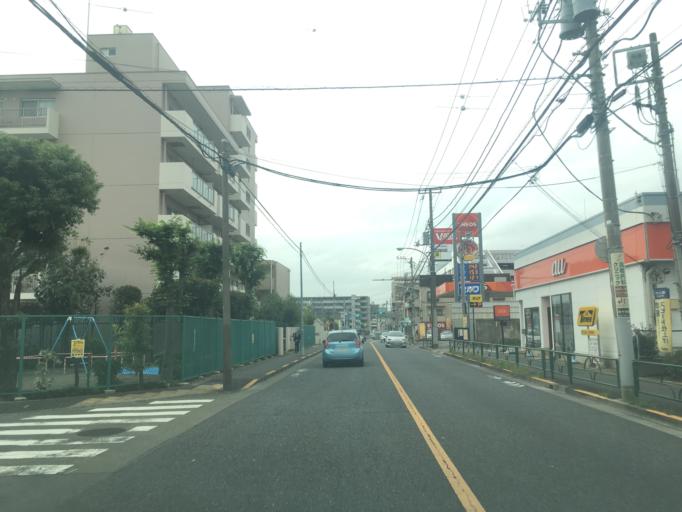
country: JP
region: Tokyo
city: Kokubunji
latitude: 35.7103
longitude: 139.4684
